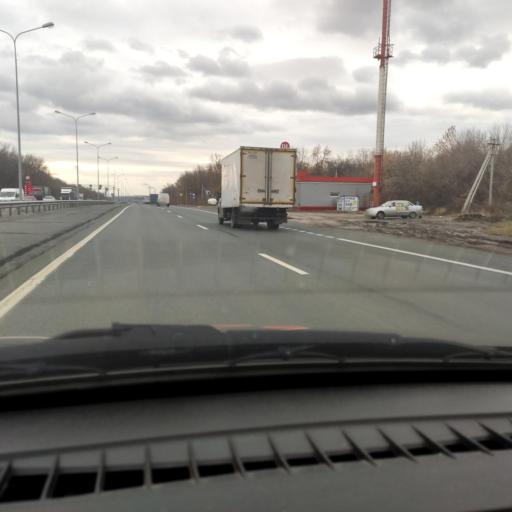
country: RU
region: Samara
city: Novosemeykino
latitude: 53.3357
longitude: 50.3015
